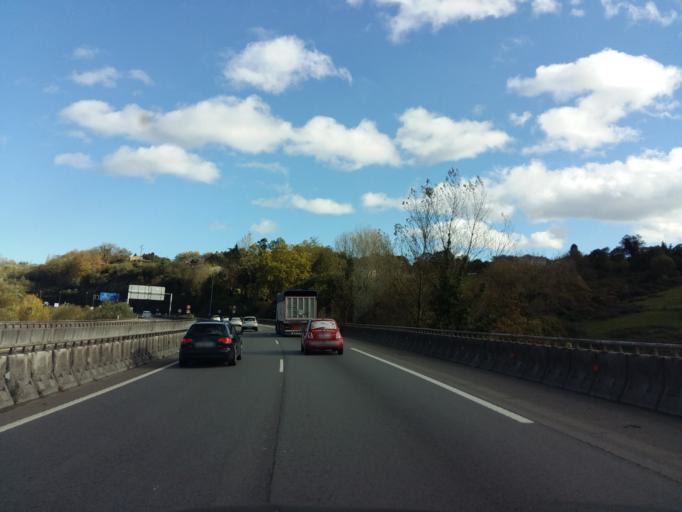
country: ES
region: Asturias
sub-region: Province of Asturias
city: Oviedo
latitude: 43.3485
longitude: -5.8439
